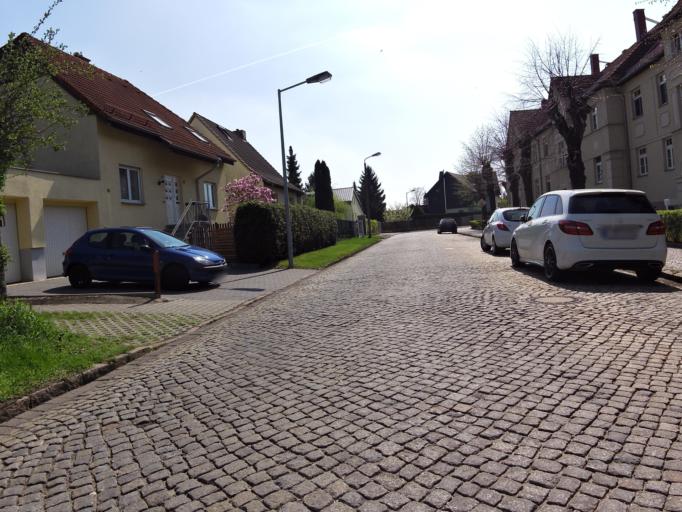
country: DE
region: Saxony
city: Leipzig
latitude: 51.3868
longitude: 12.3221
